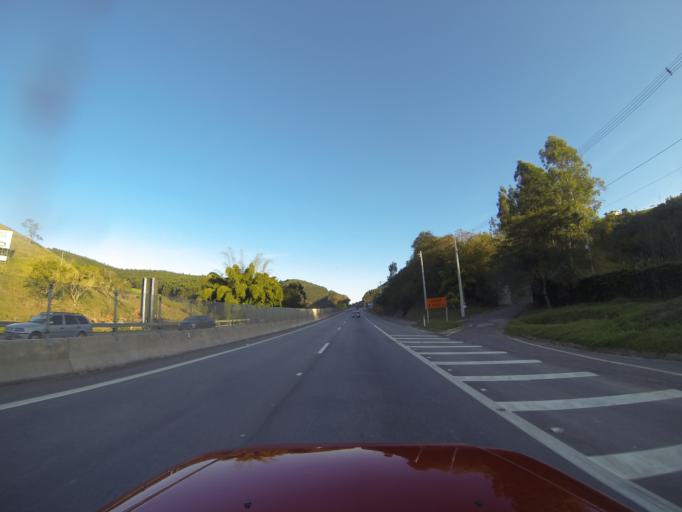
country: BR
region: Sao Paulo
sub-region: Santa Branca
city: Santa Branca
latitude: -23.3252
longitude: -45.7174
